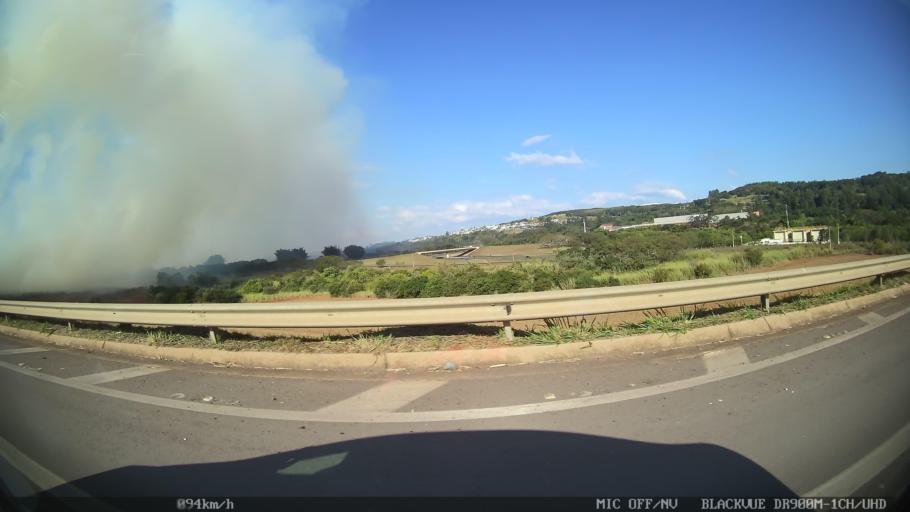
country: BR
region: Sao Paulo
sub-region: Piracicaba
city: Piracicaba
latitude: -22.6978
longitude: -47.6060
